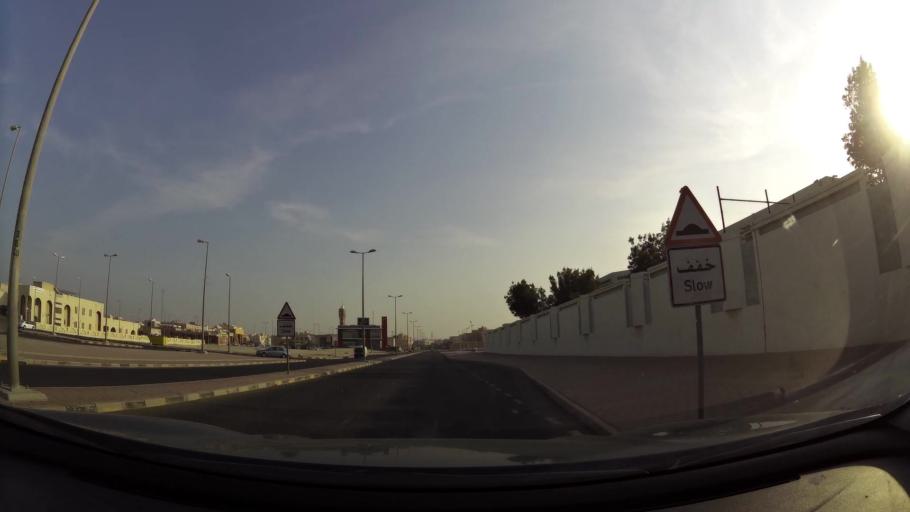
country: KW
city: Al Funaytis
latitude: 29.2374
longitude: 48.0777
